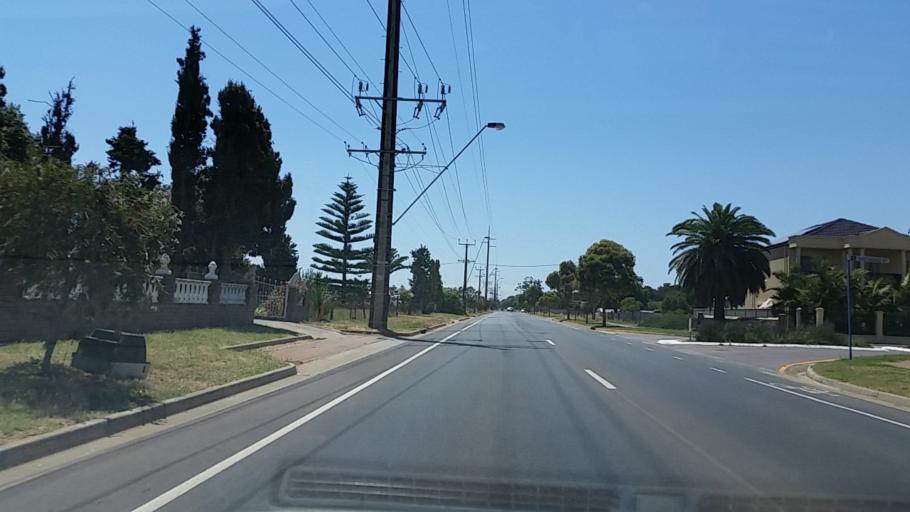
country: AU
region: South Australia
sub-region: Salisbury
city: Salisbury
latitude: -34.7867
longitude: 138.6038
